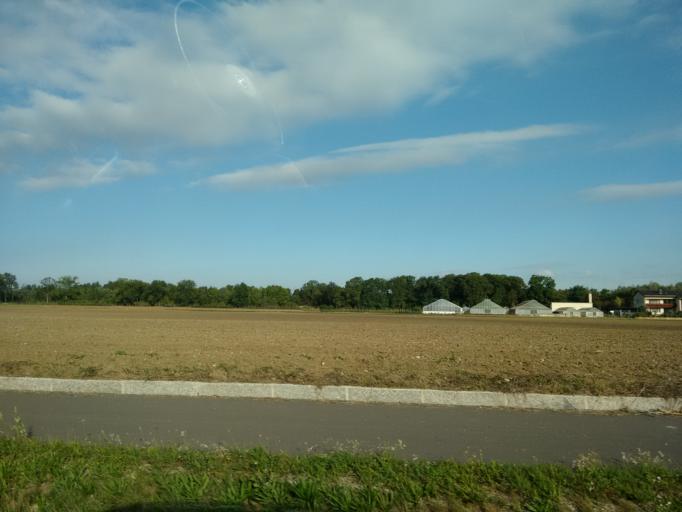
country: AT
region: Upper Austria
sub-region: Politischer Bezirk Linz-Land
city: Traun
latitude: 48.2259
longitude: 14.2079
